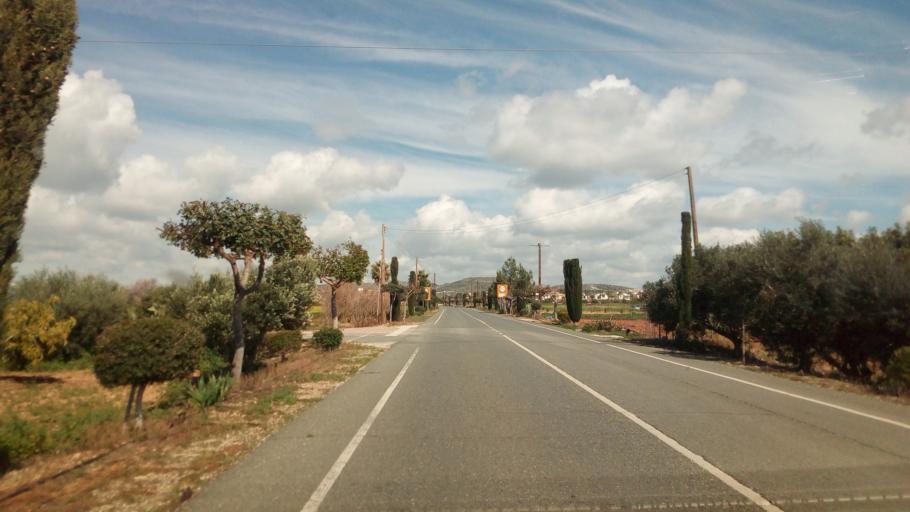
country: CY
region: Pafos
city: Mesogi
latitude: 34.7317
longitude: 32.5322
